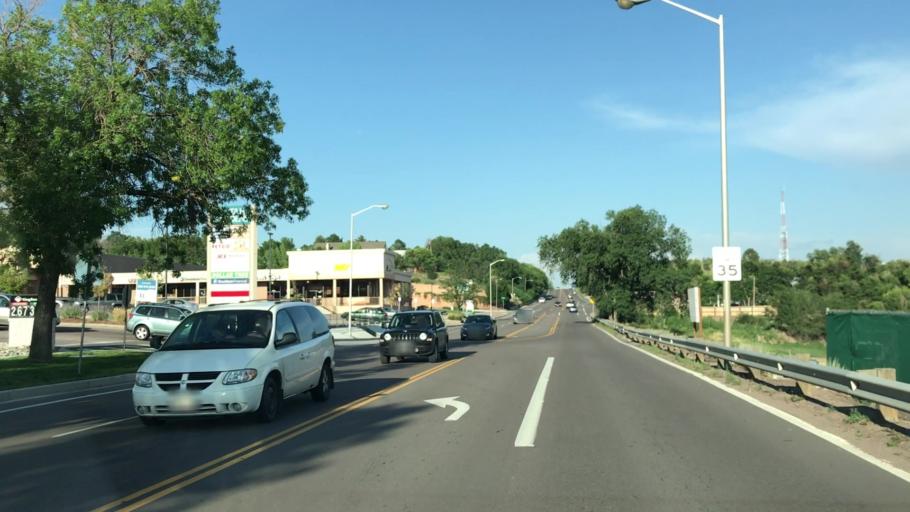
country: US
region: Colorado
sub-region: El Paso County
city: Colorado Springs
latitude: 38.8479
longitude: -104.8487
